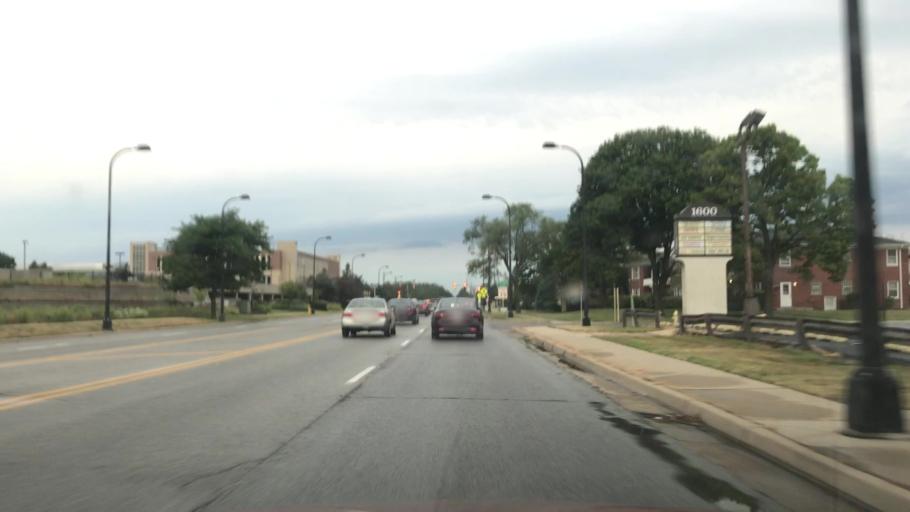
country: US
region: Illinois
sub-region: Cook County
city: Park Ridge
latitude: 42.0399
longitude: -87.8469
